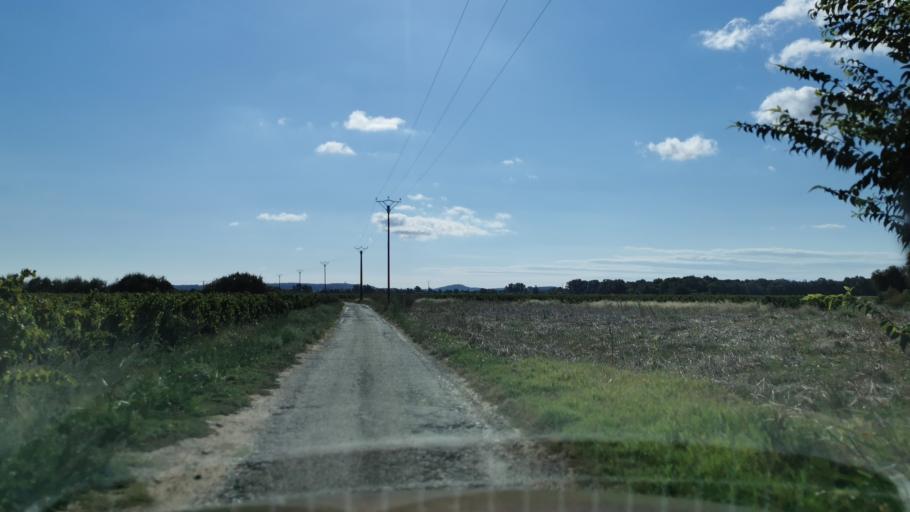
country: FR
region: Languedoc-Roussillon
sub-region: Departement de l'Aude
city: Canet
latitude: 43.2429
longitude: 2.8643
